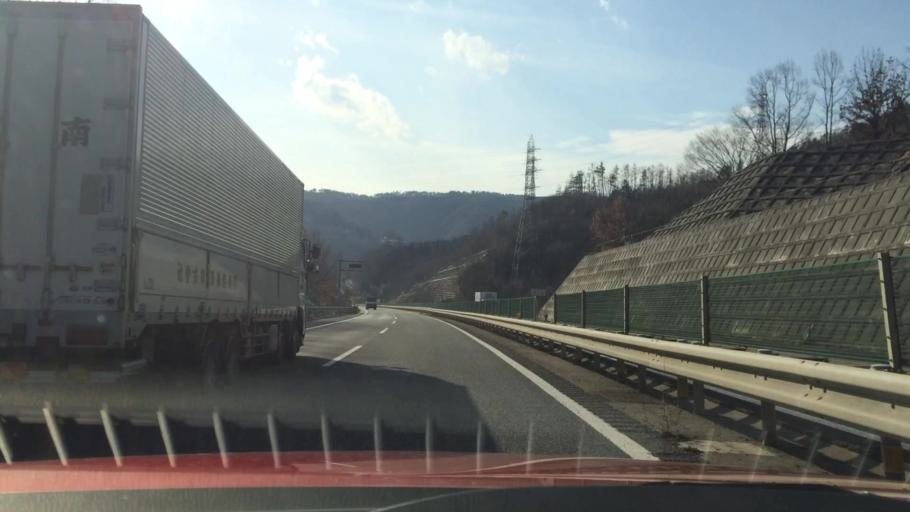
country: JP
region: Nagano
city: Toyoshina
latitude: 36.3518
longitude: 137.9686
